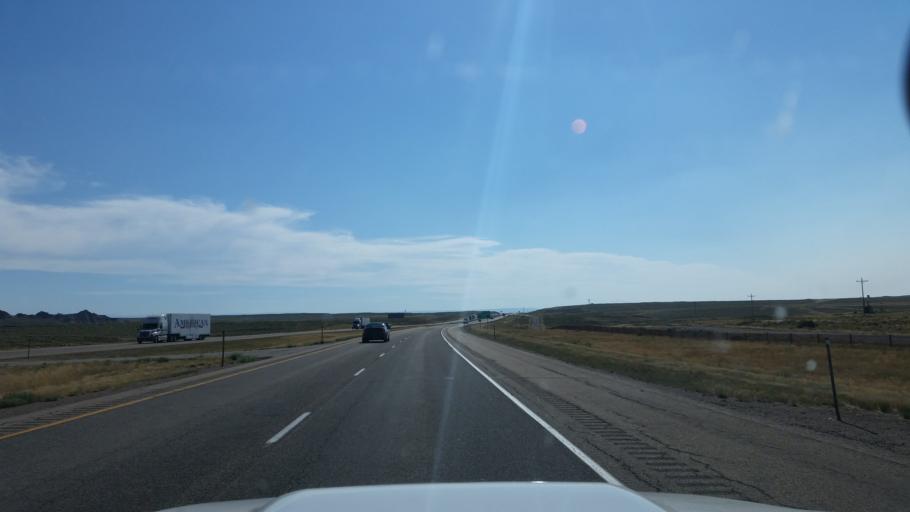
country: US
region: Wyoming
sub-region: Uinta County
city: Lyman
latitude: 41.4376
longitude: -110.0976
